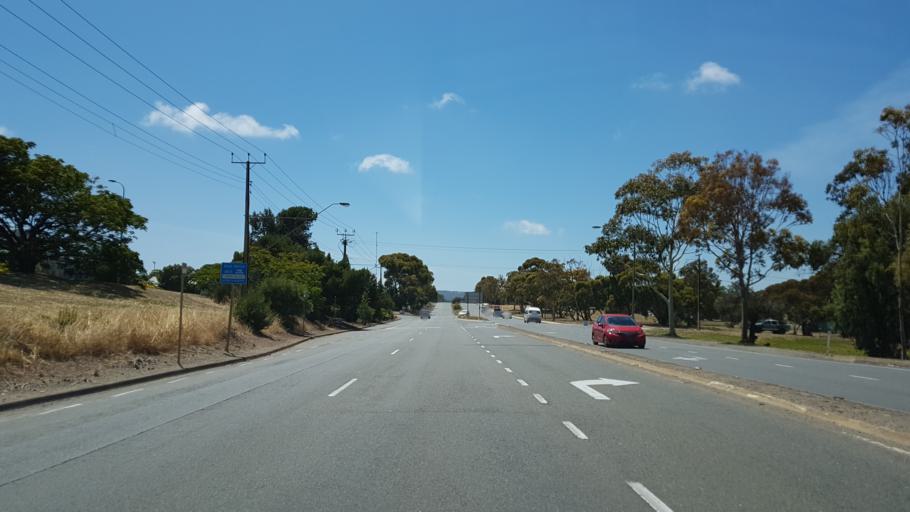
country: AU
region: South Australia
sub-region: Onkaparinga
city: Morphett Vale
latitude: -35.1064
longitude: 138.5006
